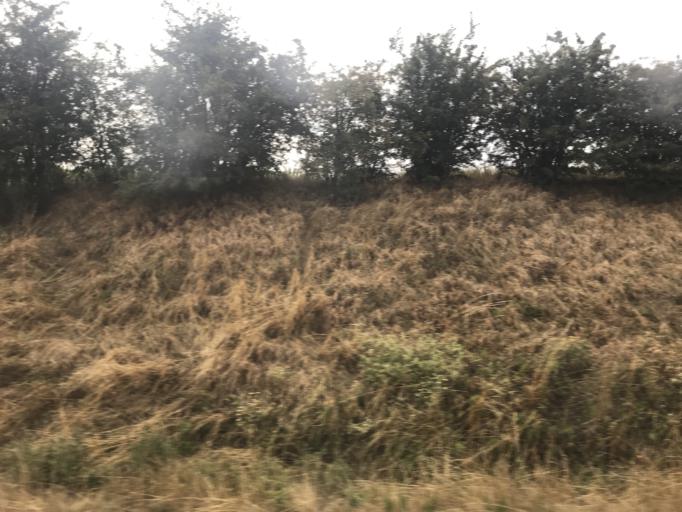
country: PL
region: Greater Poland Voivodeship
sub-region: Powiat gnieznienski
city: Lubowo
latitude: 52.5106
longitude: 17.5121
